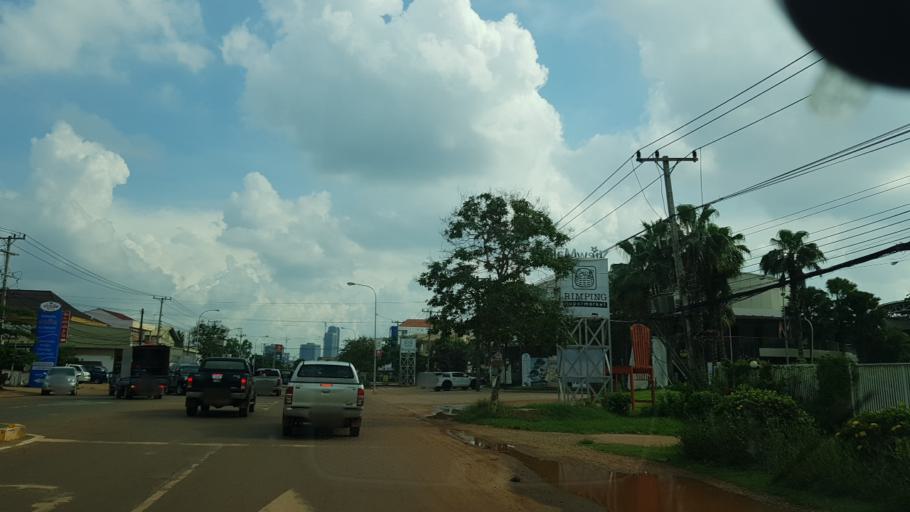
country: LA
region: Vientiane
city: Vientiane
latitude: 18.0163
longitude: 102.6500
